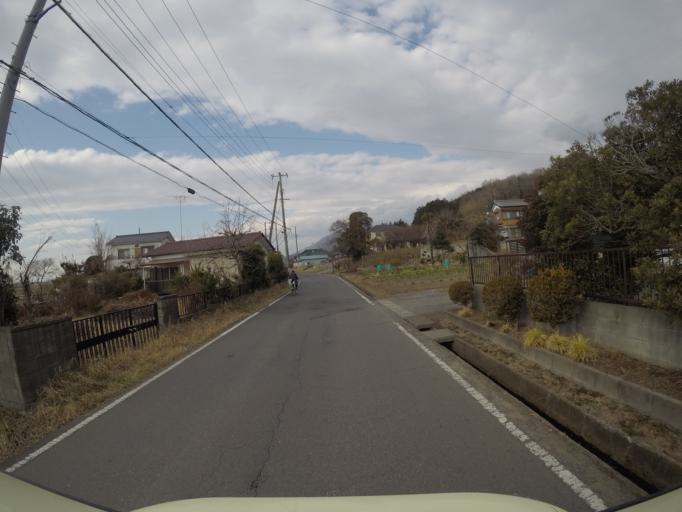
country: JP
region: Ibaraki
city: Tsukuba
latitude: 36.1602
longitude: 140.1066
